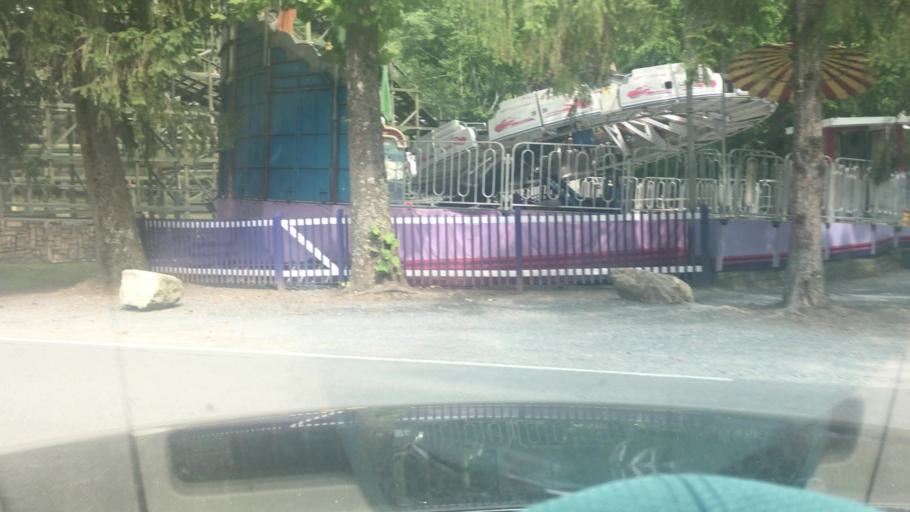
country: US
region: Pennsylvania
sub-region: Northumberland County
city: Elysburg
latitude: 40.8771
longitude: -76.5061
